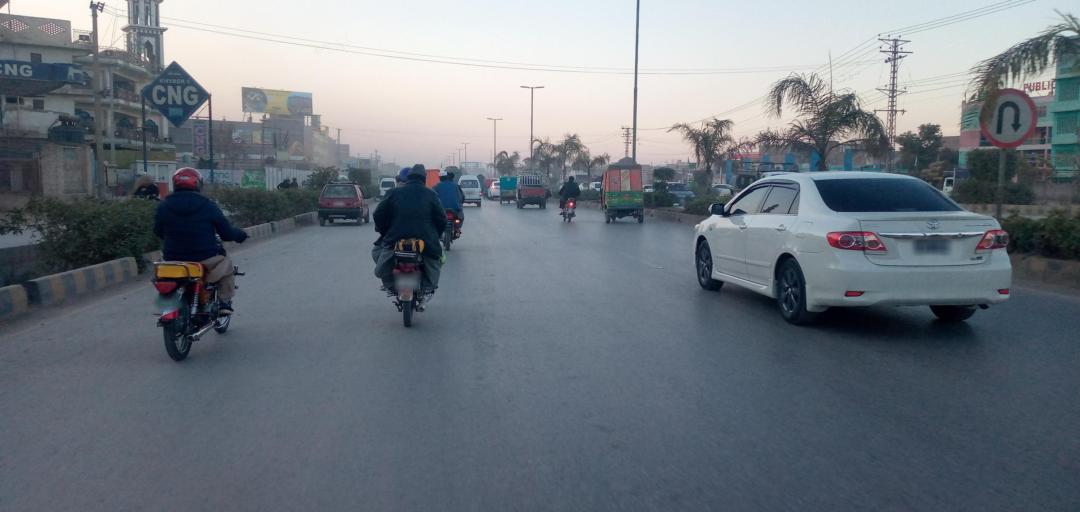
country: PK
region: Khyber Pakhtunkhwa
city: Peshawar
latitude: 34.0286
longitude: 71.6151
